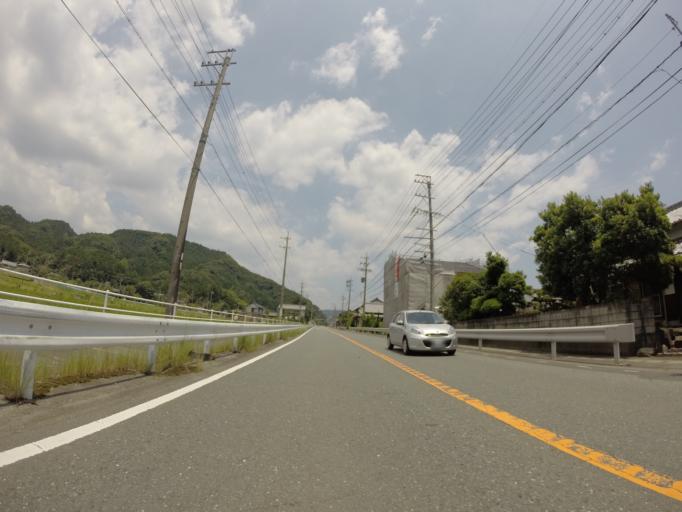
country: JP
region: Shizuoka
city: Kanaya
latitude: 34.7932
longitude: 138.0725
